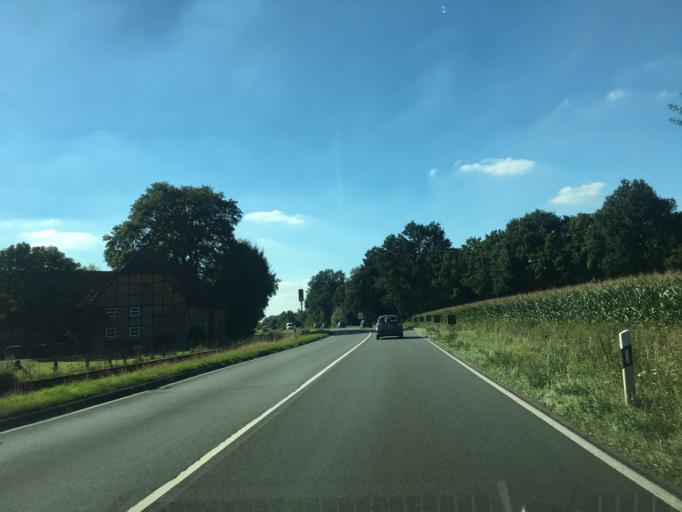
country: DE
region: North Rhine-Westphalia
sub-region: Regierungsbezirk Munster
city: Beelen
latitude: 51.9324
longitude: 8.1087
